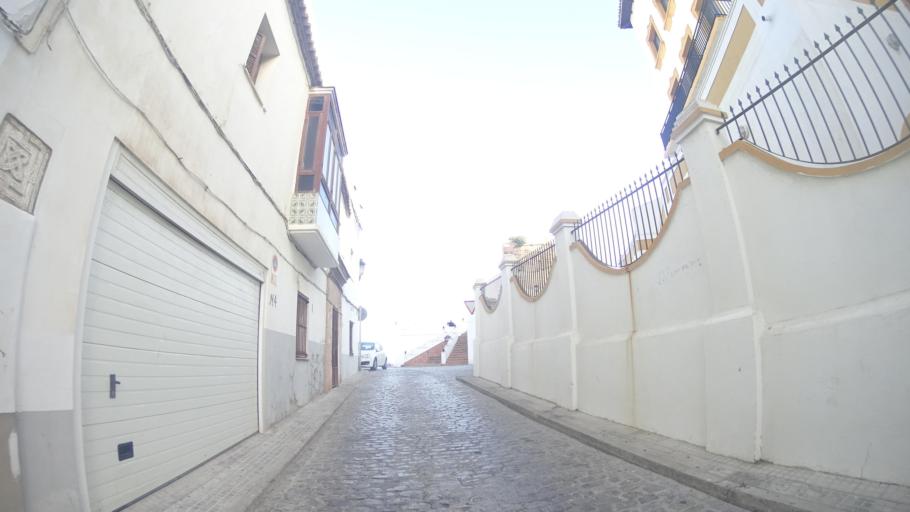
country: ES
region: Andalusia
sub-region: Provincia de Cadiz
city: Tarifa
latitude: 36.0124
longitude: -5.6011
